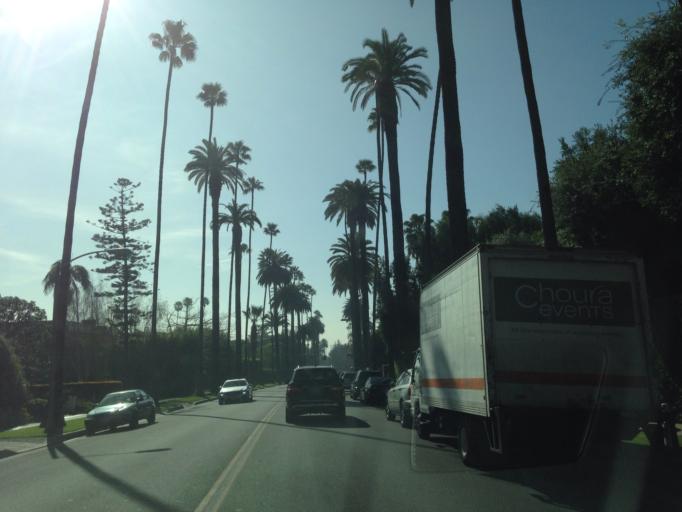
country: US
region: California
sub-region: Los Angeles County
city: Beverly Hills
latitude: 34.0838
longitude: -118.4122
